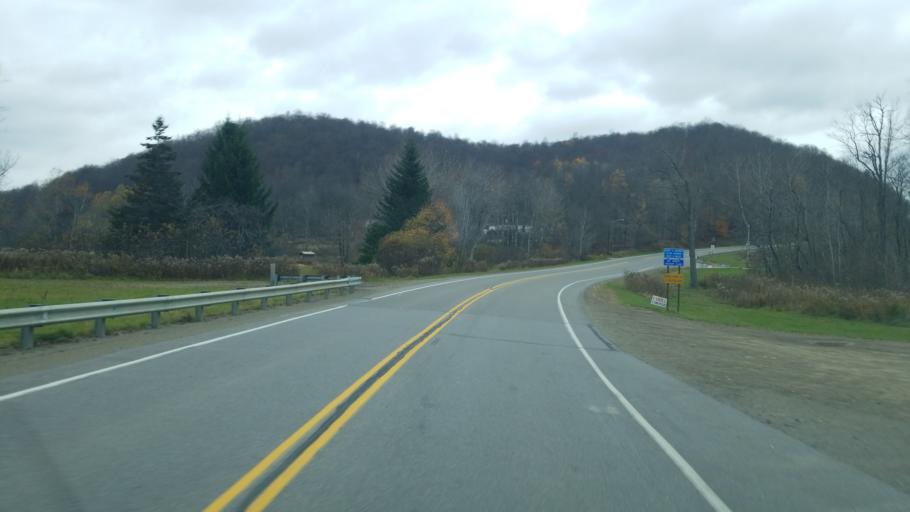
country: US
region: Pennsylvania
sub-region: McKean County
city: Smethport
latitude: 41.7051
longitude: -78.5911
